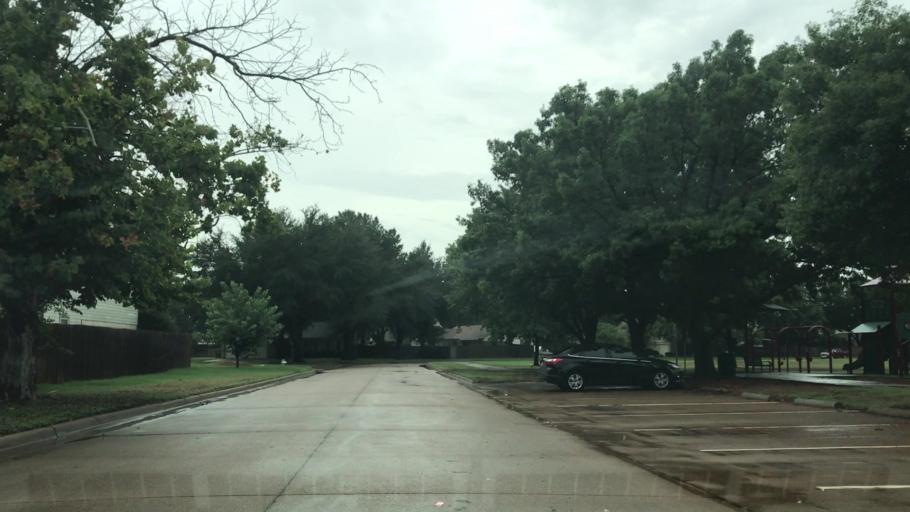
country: US
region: Texas
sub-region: Denton County
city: Flower Mound
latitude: 33.0389
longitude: -97.0537
